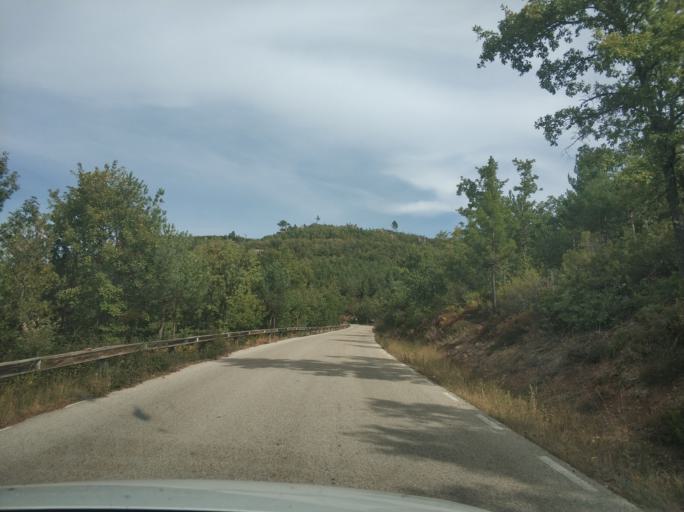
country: ES
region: Castille and Leon
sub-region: Provincia de Soria
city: Duruelo de la Sierra
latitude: 41.9053
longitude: -2.9420
